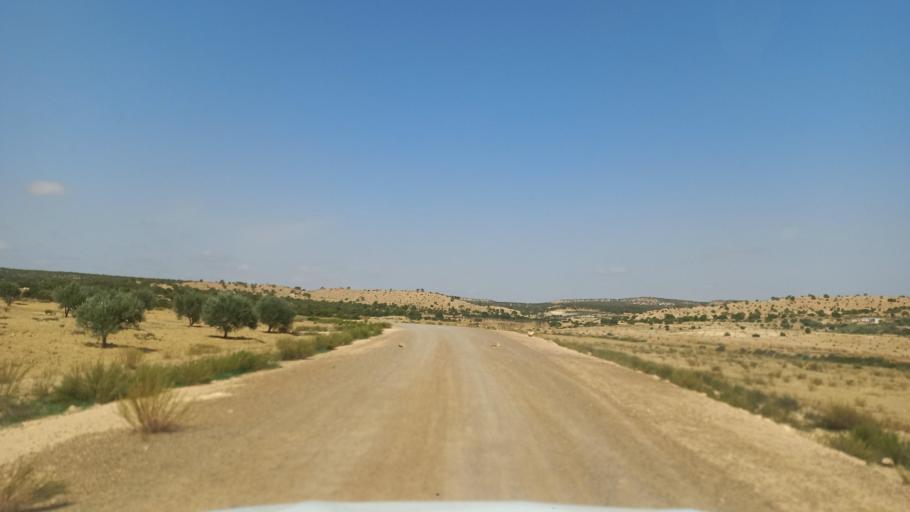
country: TN
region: Al Qasrayn
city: Sbiba
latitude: 35.3891
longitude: 8.9552
